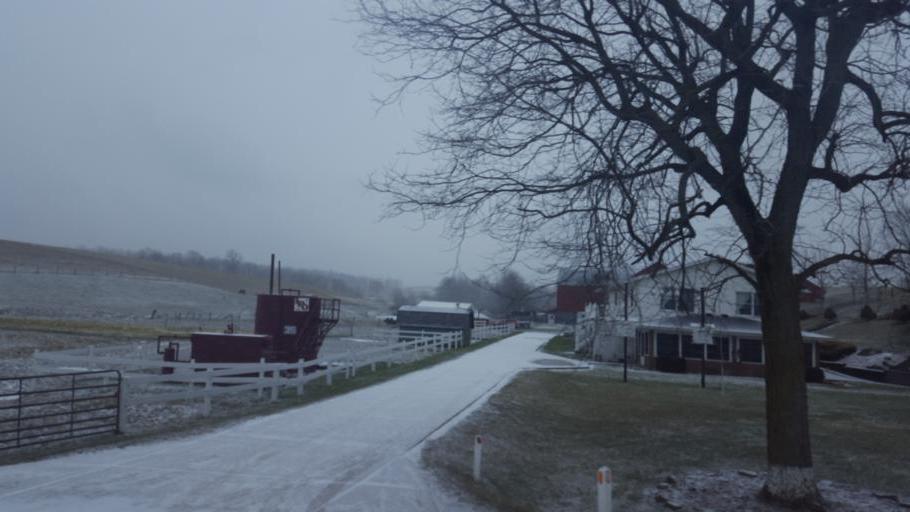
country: US
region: Ohio
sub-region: Tuscarawas County
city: Sugarcreek
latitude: 40.4660
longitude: -81.7339
